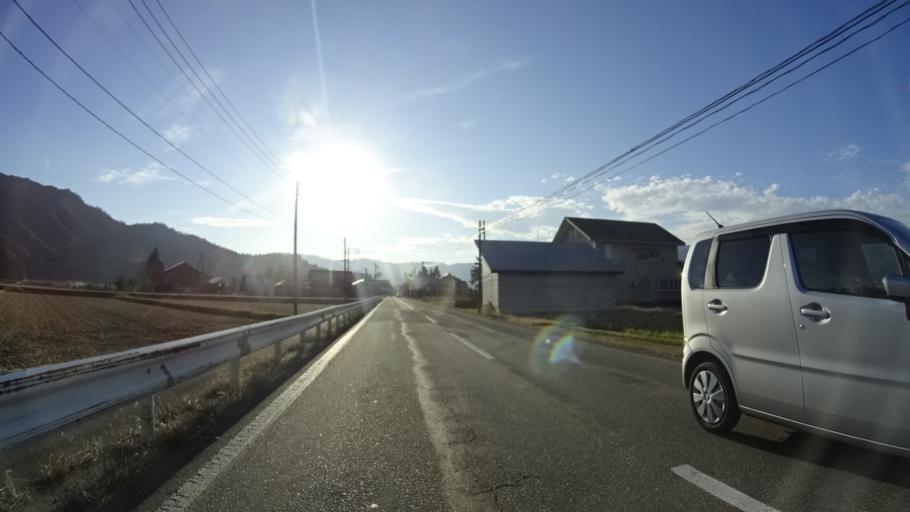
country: JP
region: Niigata
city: Shiozawa
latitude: 37.0096
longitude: 138.8486
